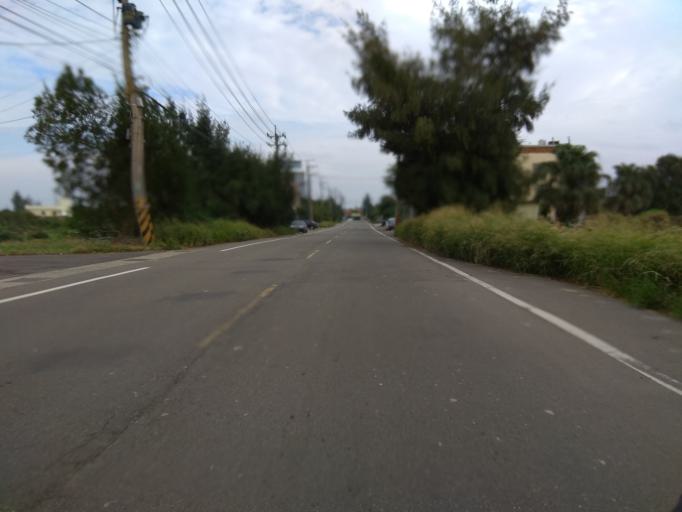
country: TW
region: Taiwan
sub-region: Hsinchu
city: Zhubei
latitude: 24.9848
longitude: 121.0412
